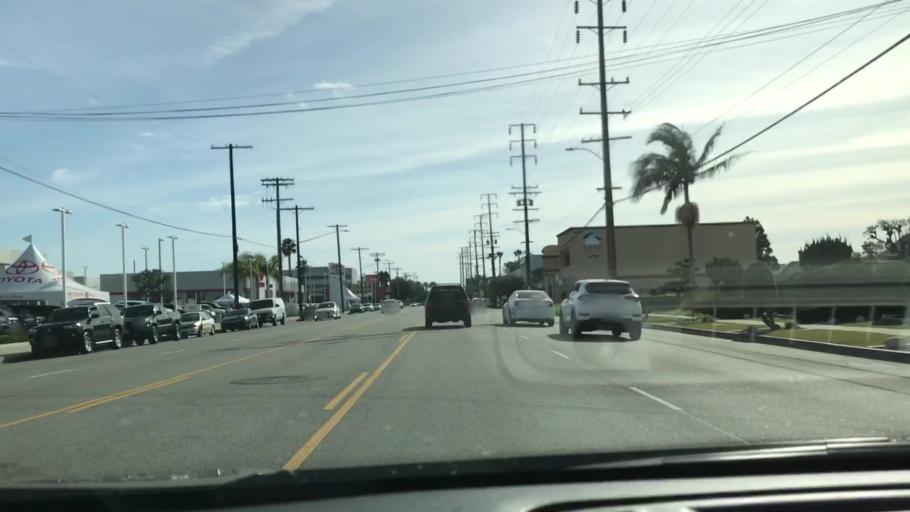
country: US
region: California
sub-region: Los Angeles County
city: Gardena
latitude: 33.8643
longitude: -118.3092
